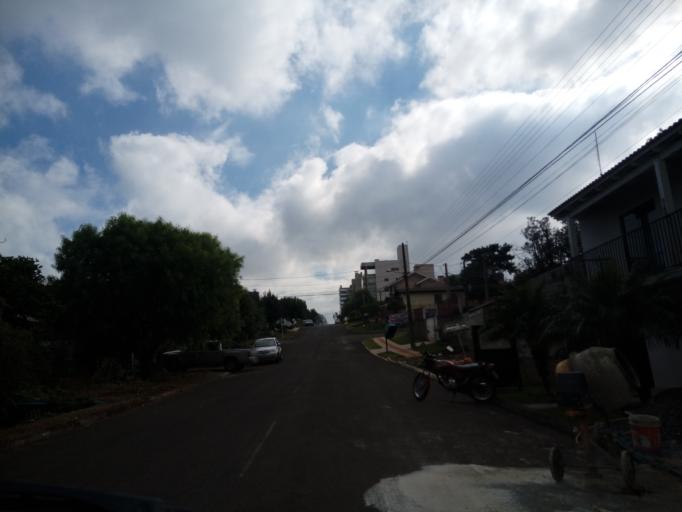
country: BR
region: Santa Catarina
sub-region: Chapeco
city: Chapeco
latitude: -27.0946
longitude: -52.5991
